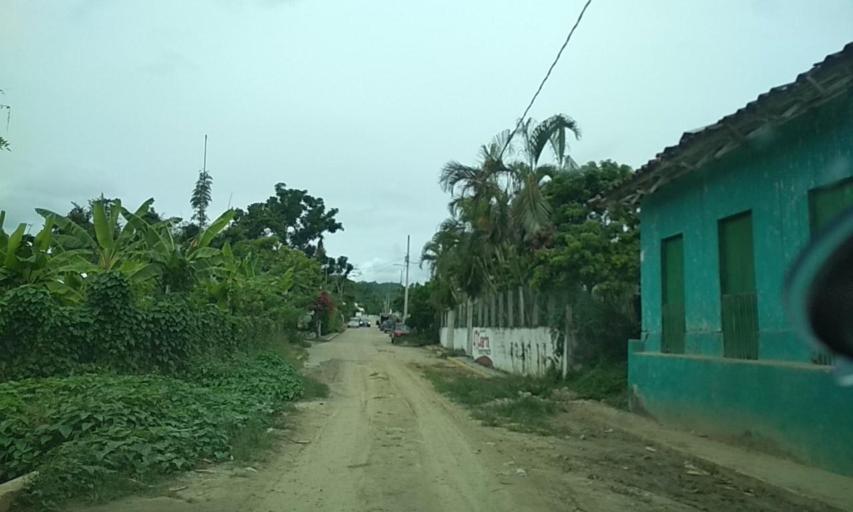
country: MX
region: Veracruz
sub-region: Papantla
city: Residencial Tajin
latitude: 20.5989
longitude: -97.3340
